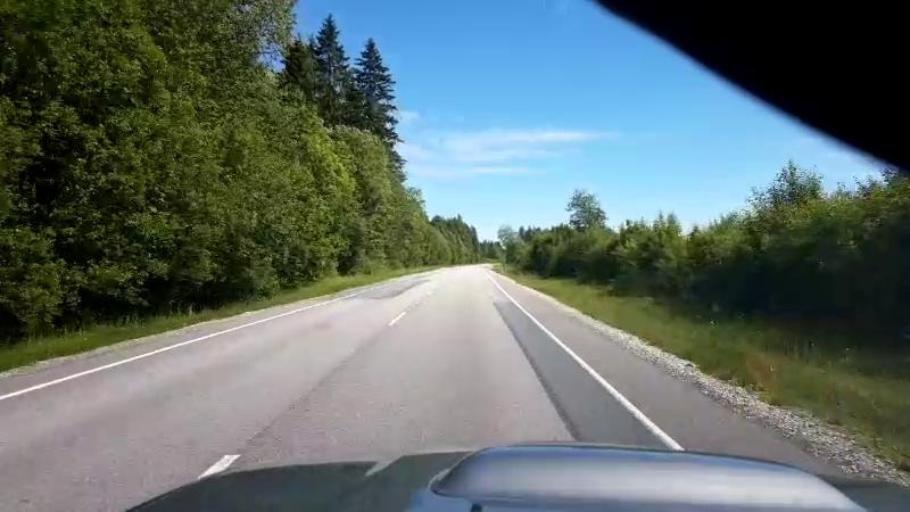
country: EE
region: Jaervamaa
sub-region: Koeru vald
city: Koeru
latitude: 58.9736
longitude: 26.1224
